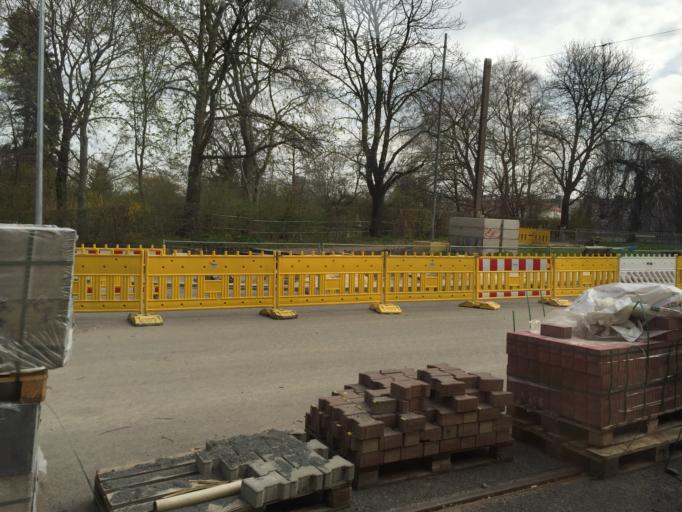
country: DE
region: Saxony
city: Dresden
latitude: 51.0590
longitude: 13.7530
